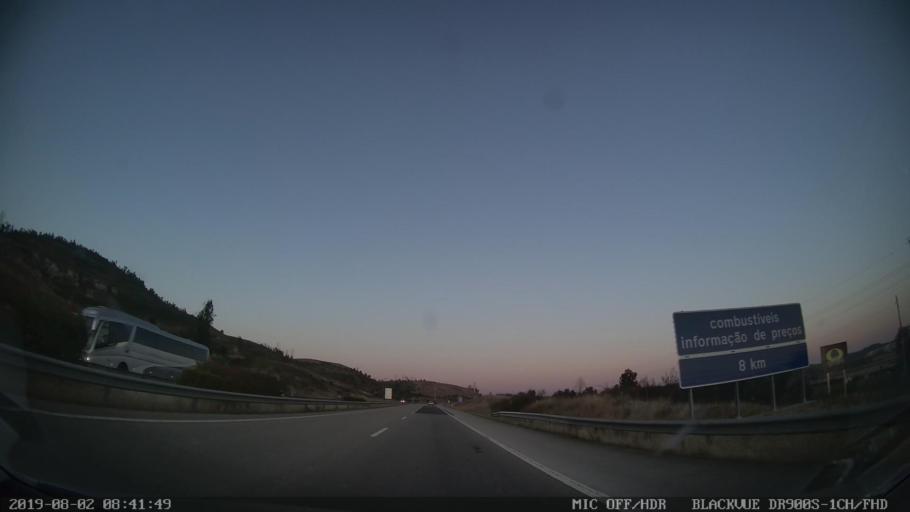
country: PT
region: Santarem
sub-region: Abrantes
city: Tramagal
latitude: 39.4847
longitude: -8.2540
